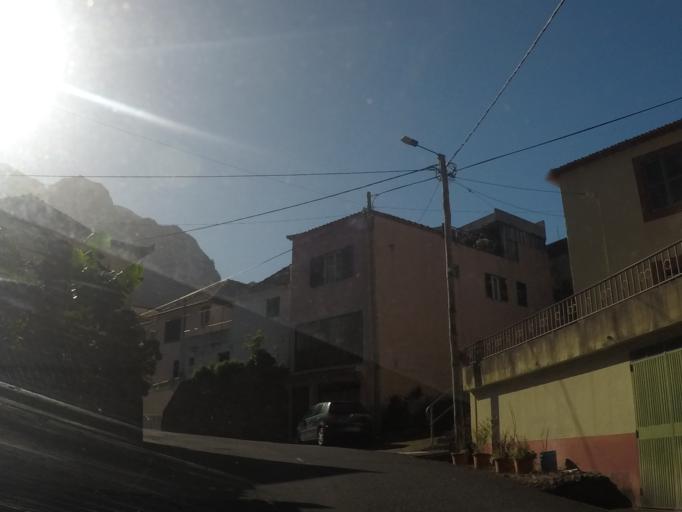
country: PT
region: Madeira
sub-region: Sao Vicente
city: Sao Vicente
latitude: 32.8033
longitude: -16.9651
